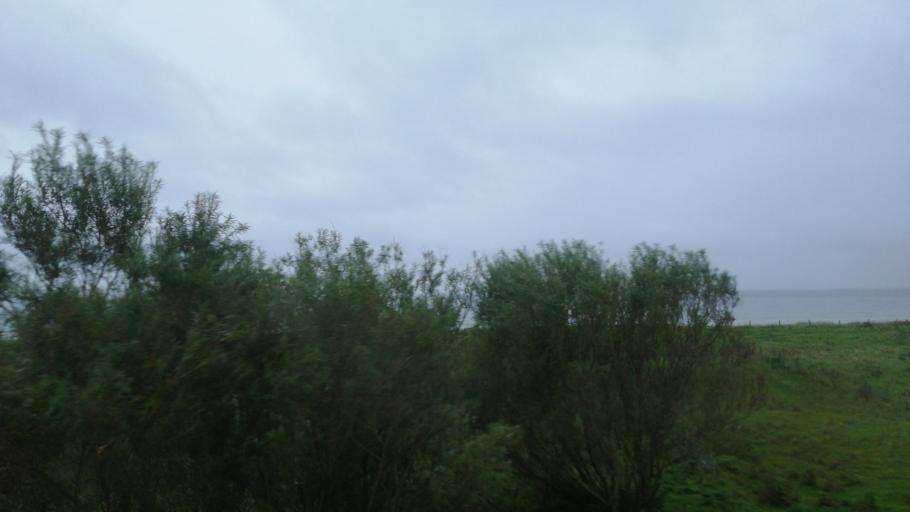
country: GB
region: Scotland
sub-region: Highland
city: Brora
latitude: 58.0516
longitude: -3.8121
